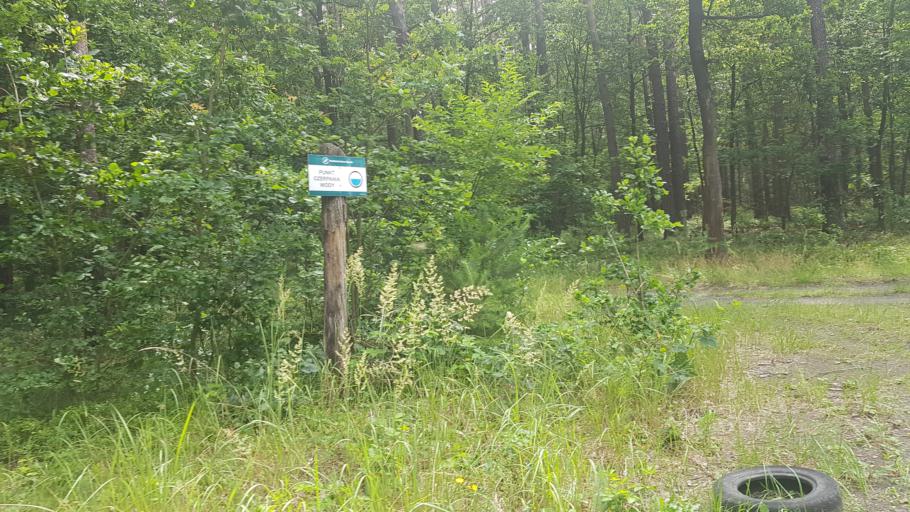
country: PL
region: Opole Voivodeship
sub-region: Powiat opolski
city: Chrzastowice
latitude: 50.6976
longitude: 18.1290
